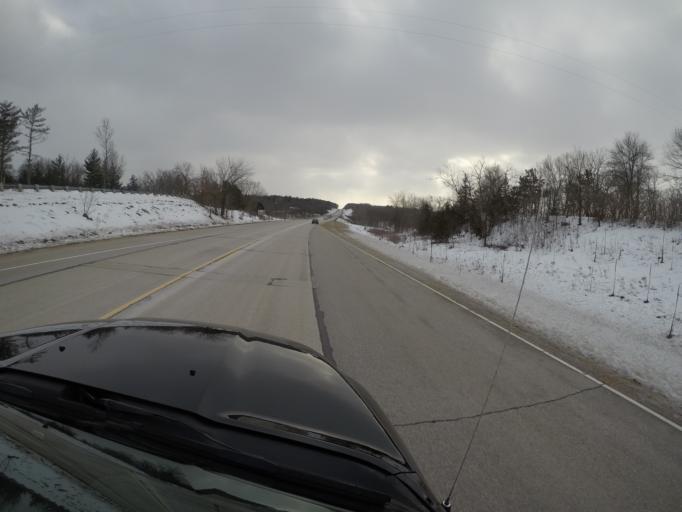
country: US
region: Wisconsin
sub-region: Trempealeau County
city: Galesville
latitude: 44.0645
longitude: -91.2912
